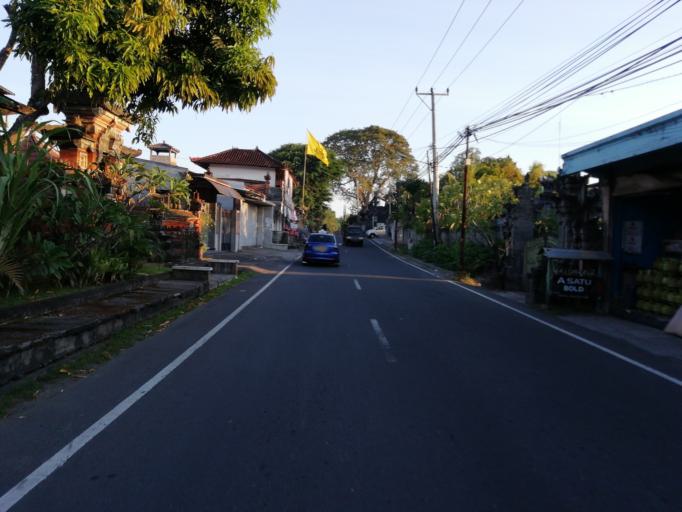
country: ID
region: Bali
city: Jimbaran
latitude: -8.8285
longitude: 115.1655
